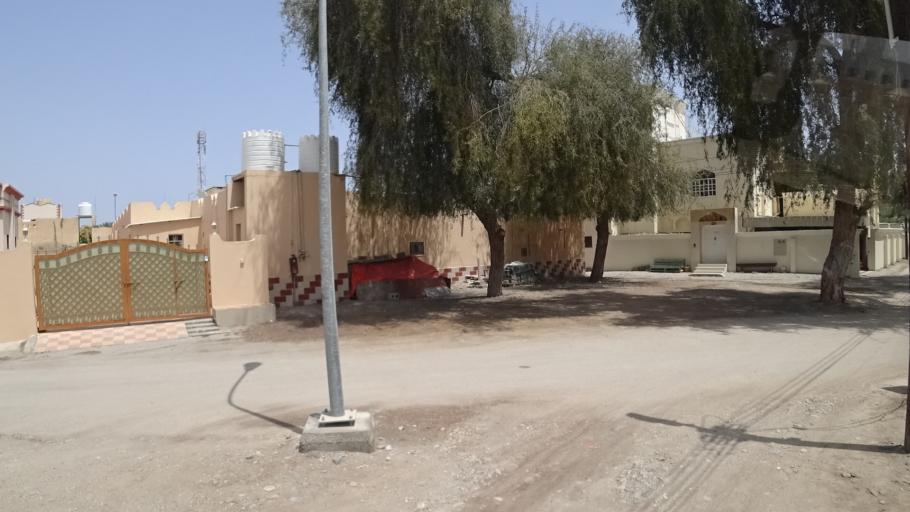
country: OM
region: Muhafazat Masqat
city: Muscat
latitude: 23.2613
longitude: 58.9141
